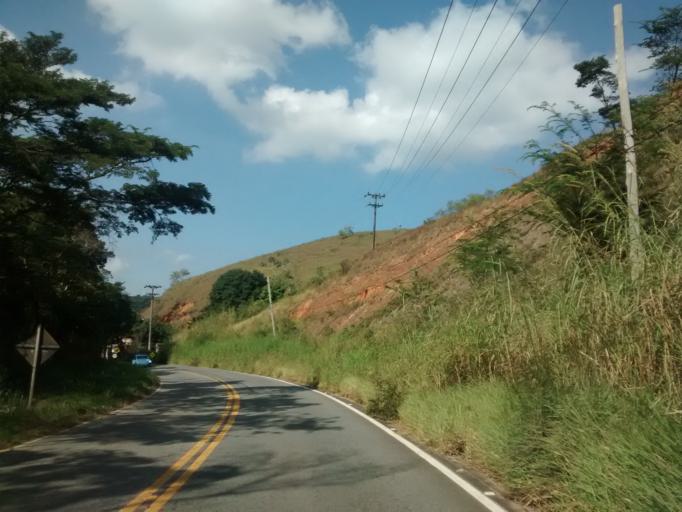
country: BR
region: Rio de Janeiro
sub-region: Miguel Pereira
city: Miguel Pereira
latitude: -22.4727
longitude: -43.5507
